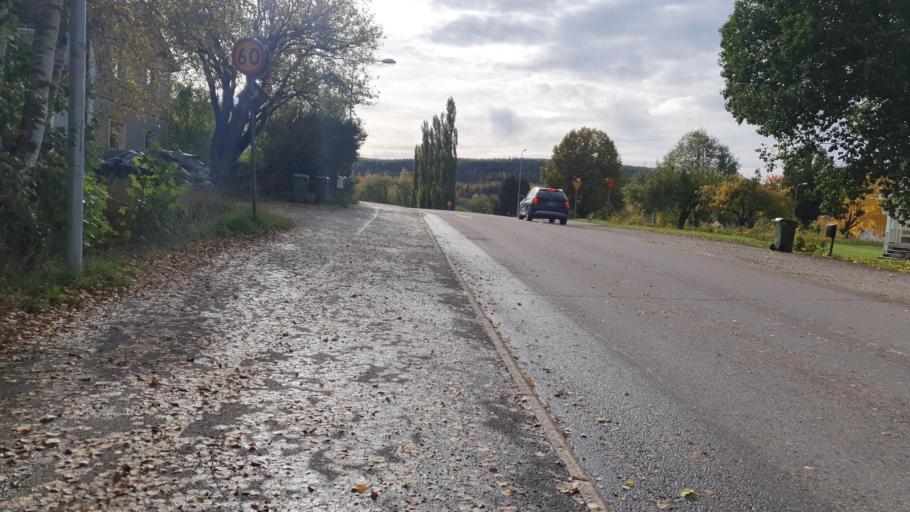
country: SE
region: Vaesternorrland
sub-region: Sundsvalls Kommun
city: Sundsvall
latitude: 62.4057
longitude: 17.2449
